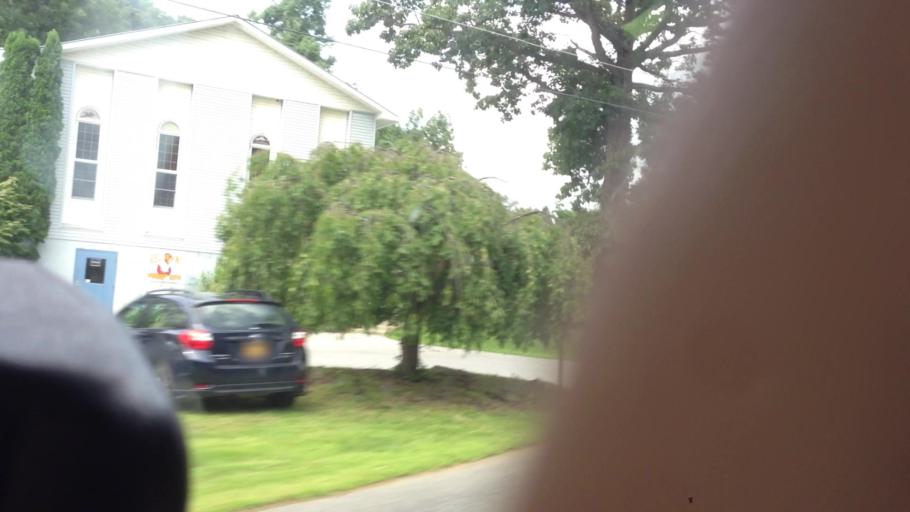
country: US
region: New York
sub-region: Dutchess County
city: Red Hook
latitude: 41.9926
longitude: -73.8693
